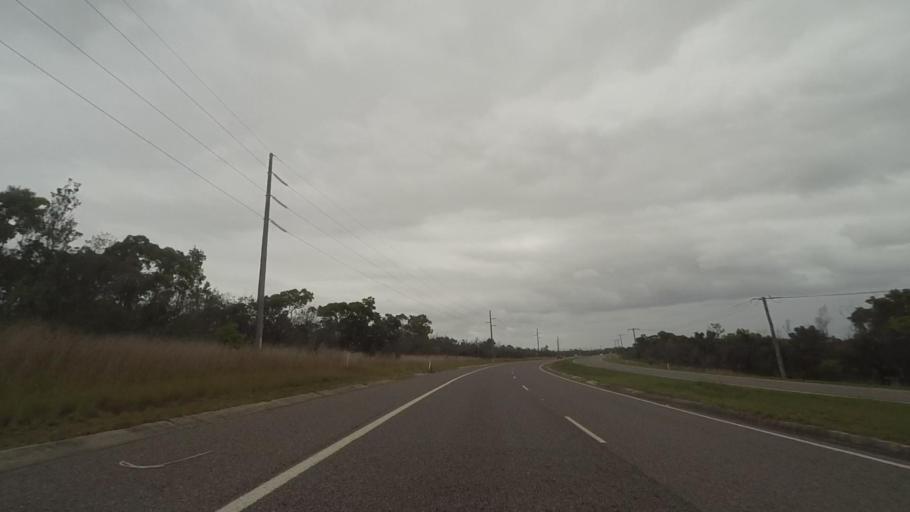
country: AU
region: New South Wales
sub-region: Wyong Shire
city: Kingfisher Shores
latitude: -33.1848
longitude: 151.5899
